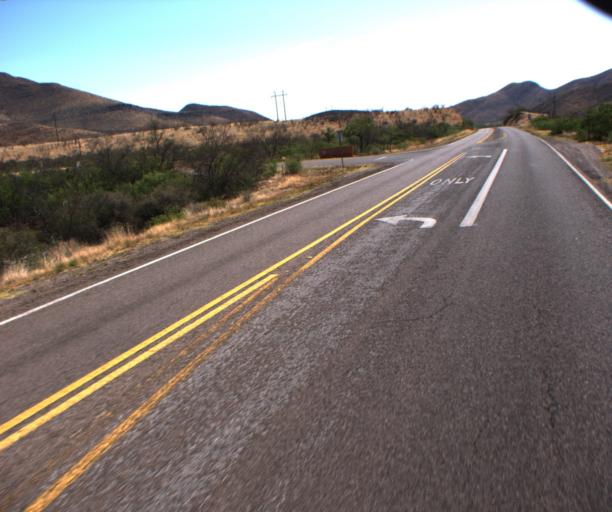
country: US
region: Arizona
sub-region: Cochise County
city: Bisbee
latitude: 31.4298
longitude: -109.8693
